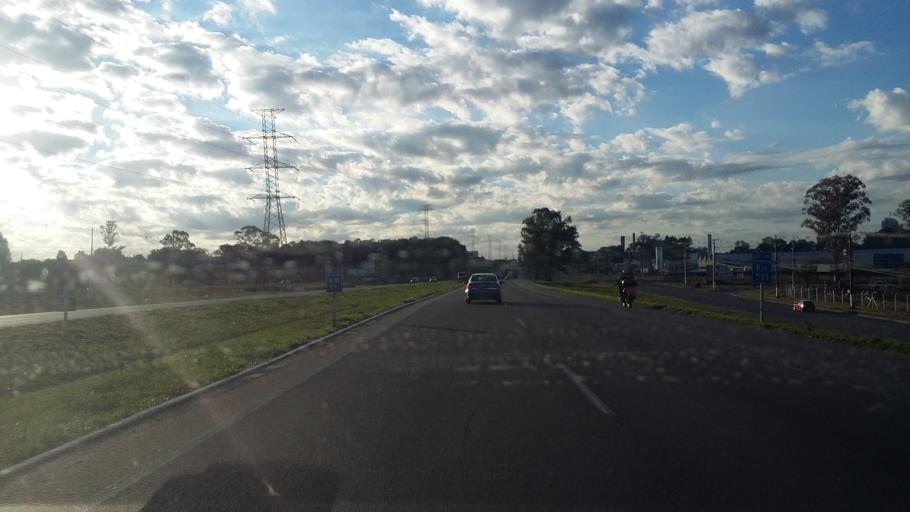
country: BR
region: Parana
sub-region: Curitiba
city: Curitiba
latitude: -25.4672
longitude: -49.3559
